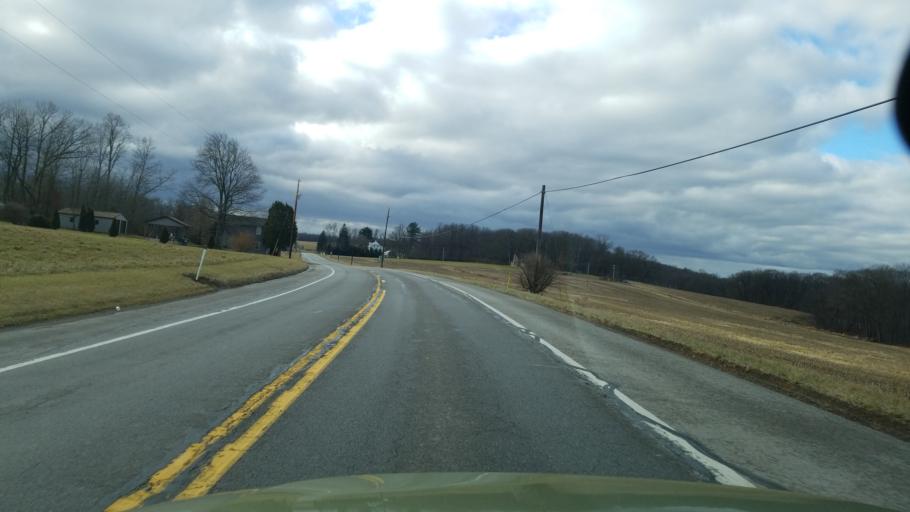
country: US
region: Pennsylvania
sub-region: Jefferson County
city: Punxsutawney
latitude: 40.8478
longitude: -79.0368
